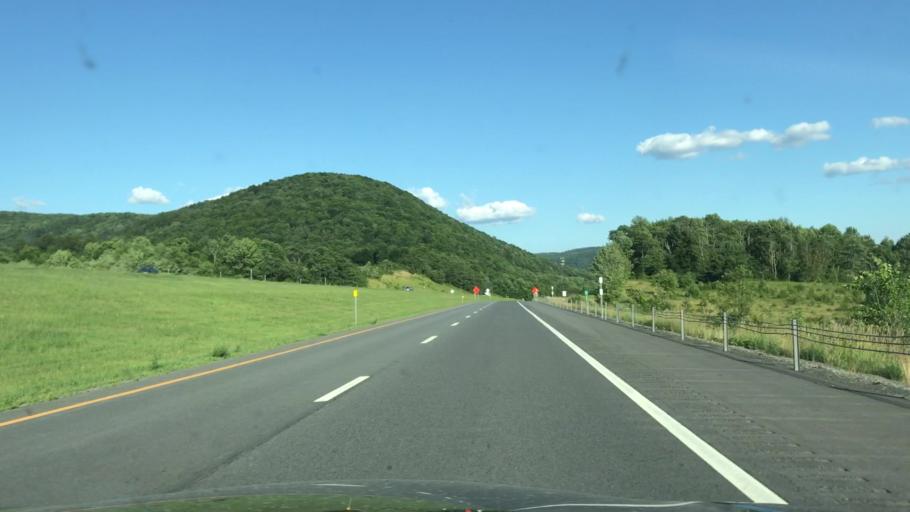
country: US
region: New York
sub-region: Sullivan County
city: Livingston Manor
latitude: 41.9627
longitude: -74.9976
